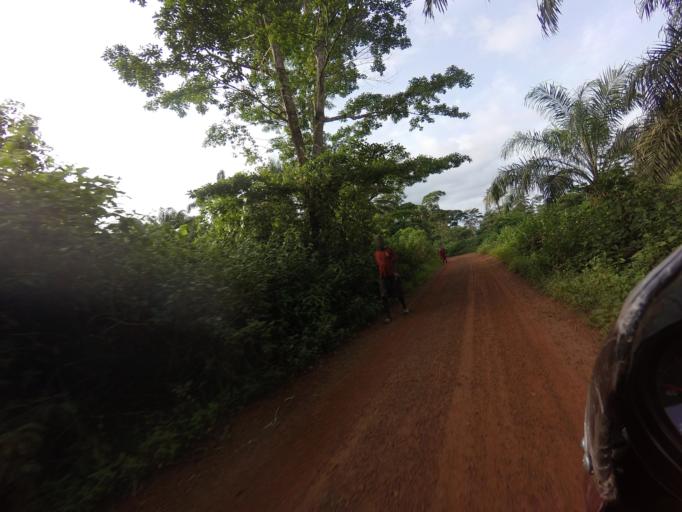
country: SL
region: Eastern Province
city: Jojoima
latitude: 7.8371
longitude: -10.8094
